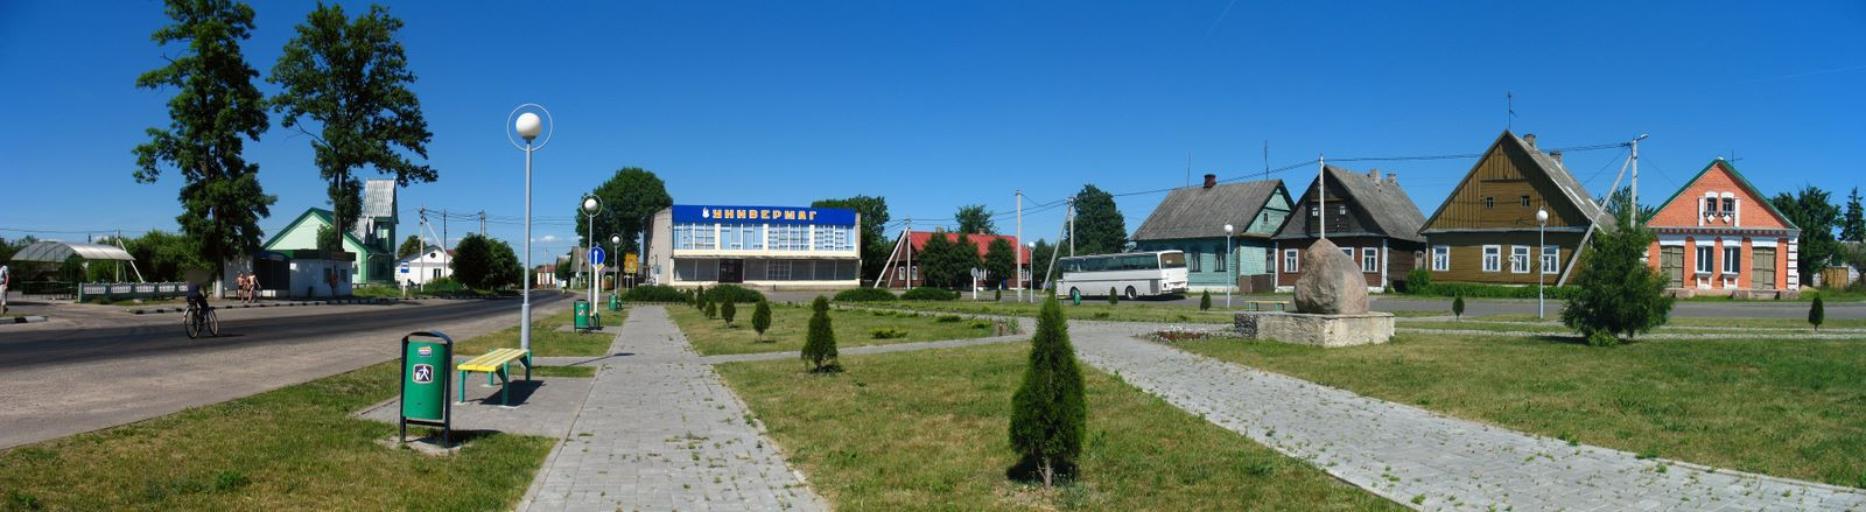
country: BY
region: Brest
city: Pruzhany
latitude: 52.5554
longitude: 24.2151
